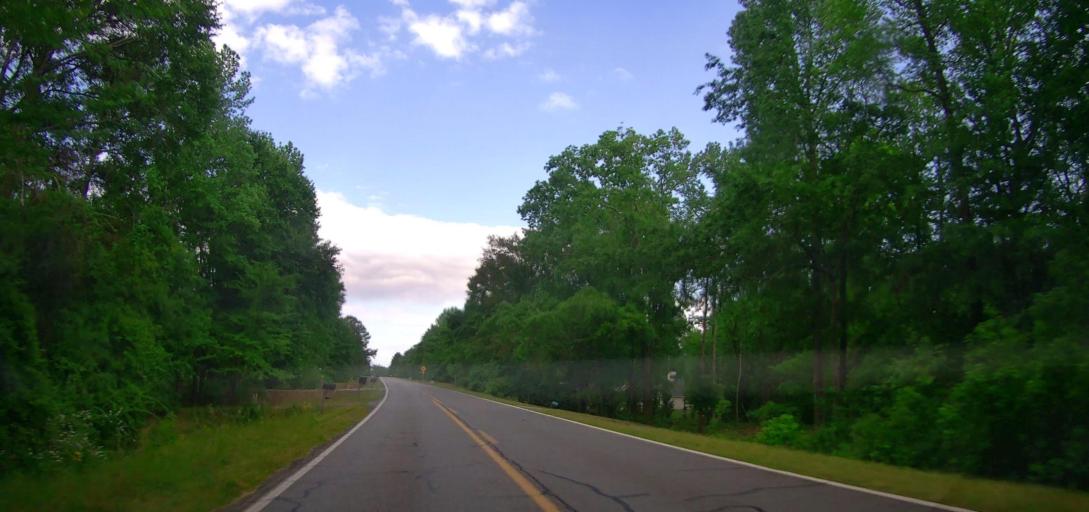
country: US
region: Georgia
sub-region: Baldwin County
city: Hardwick
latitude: 33.0614
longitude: -83.1357
